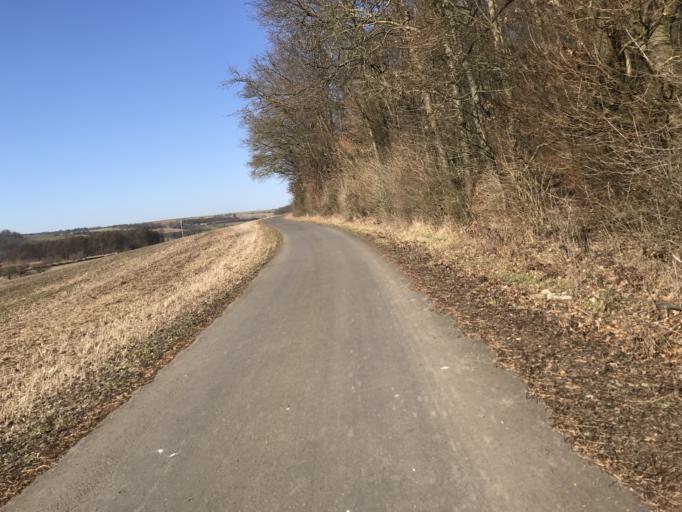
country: DE
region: Hesse
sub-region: Regierungsbezirk Darmstadt
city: Ranstadt
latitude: 50.3825
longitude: 8.9841
